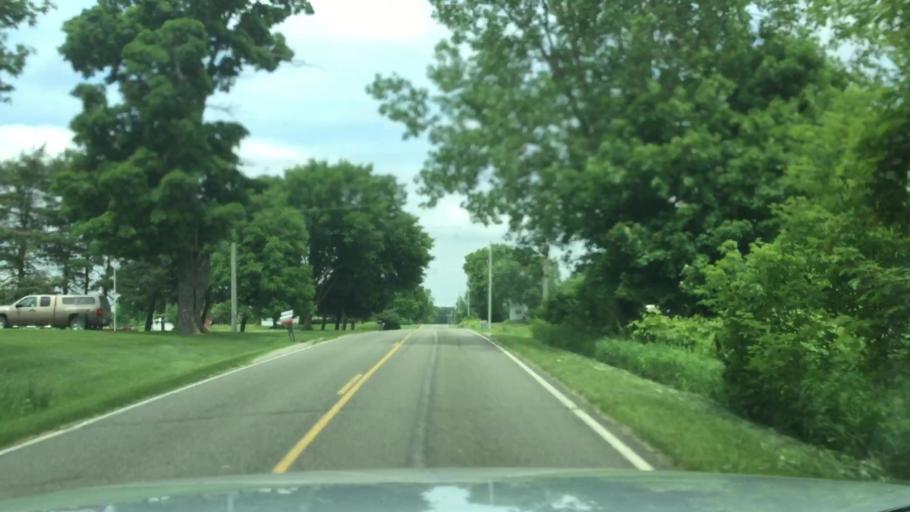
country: US
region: Michigan
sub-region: Shiawassee County
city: Durand
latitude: 42.9447
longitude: -83.9591
